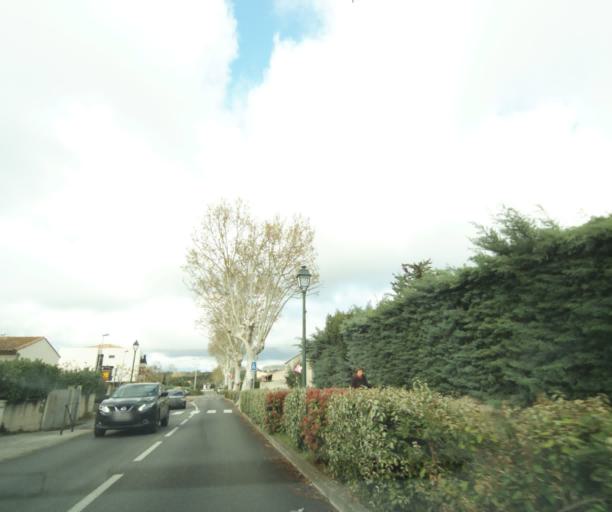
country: FR
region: Languedoc-Roussillon
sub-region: Departement de l'Herault
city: Laverune
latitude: 43.5860
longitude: 3.8089
